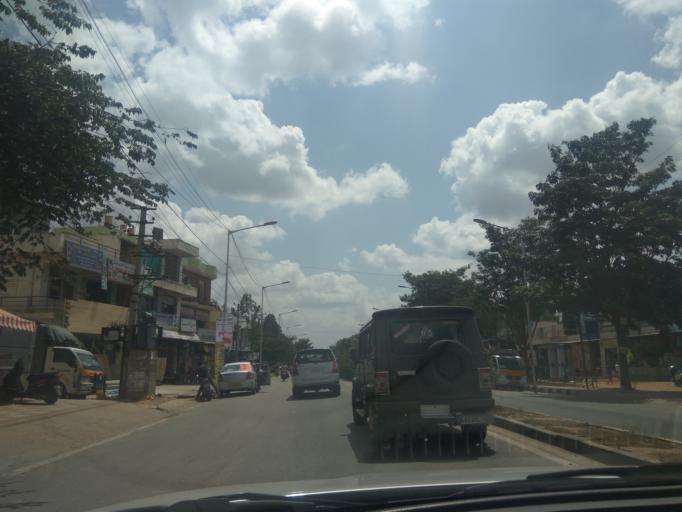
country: IN
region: Karnataka
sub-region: Bangalore Urban
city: Yelahanka
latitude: 13.1218
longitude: 77.6258
